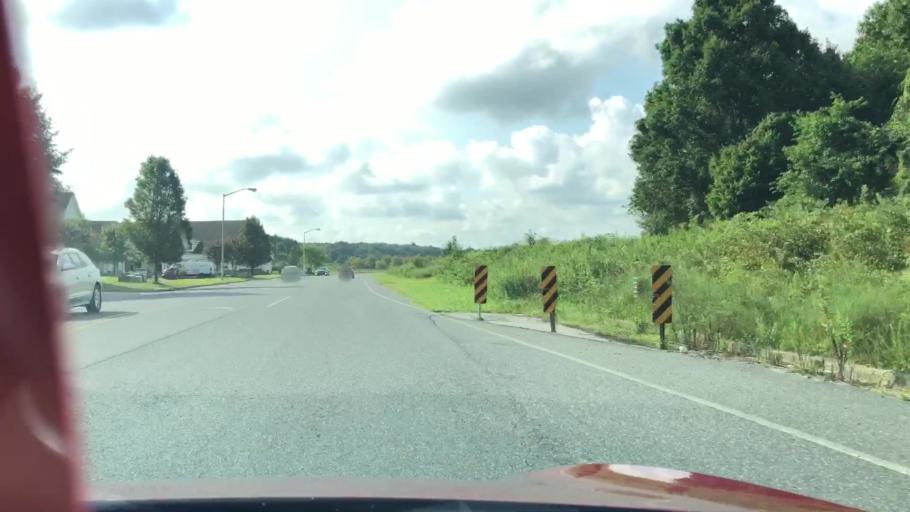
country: US
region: Maryland
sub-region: Wicomico County
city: Delmar
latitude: 38.4075
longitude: -75.5636
